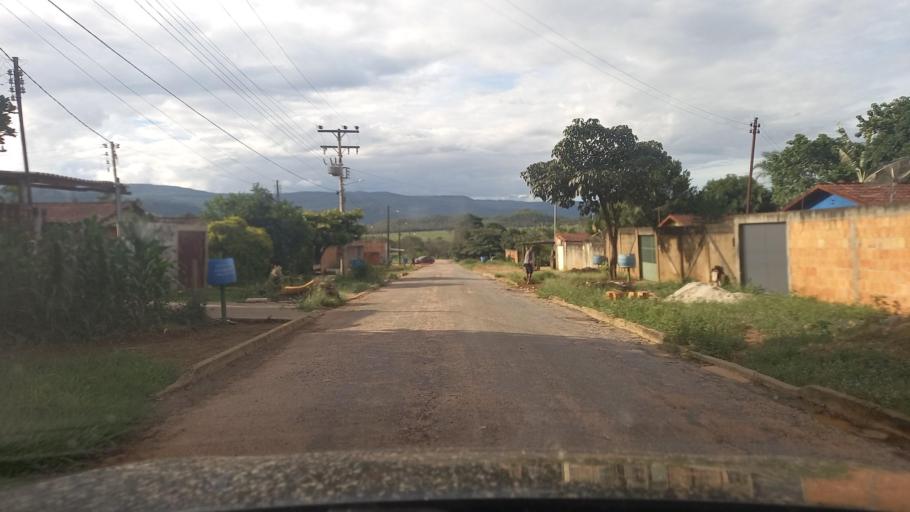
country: BR
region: Goias
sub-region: Cavalcante
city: Cavalcante
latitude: -13.7965
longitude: -47.4445
